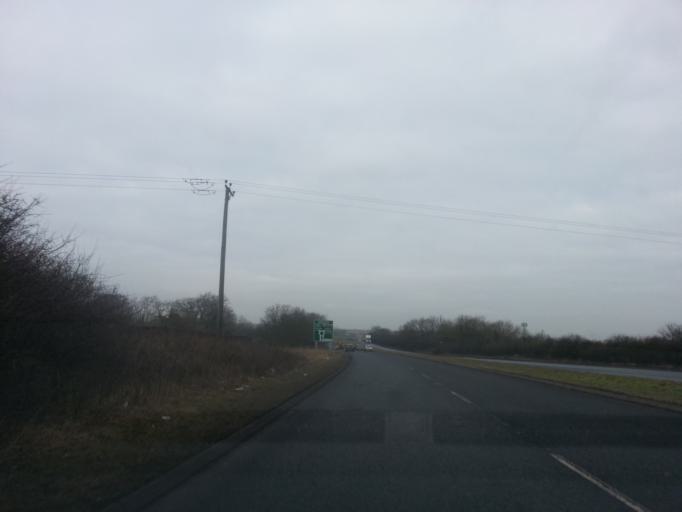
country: GB
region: England
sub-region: Darlington
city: Heighington
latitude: 54.5735
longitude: -1.6107
